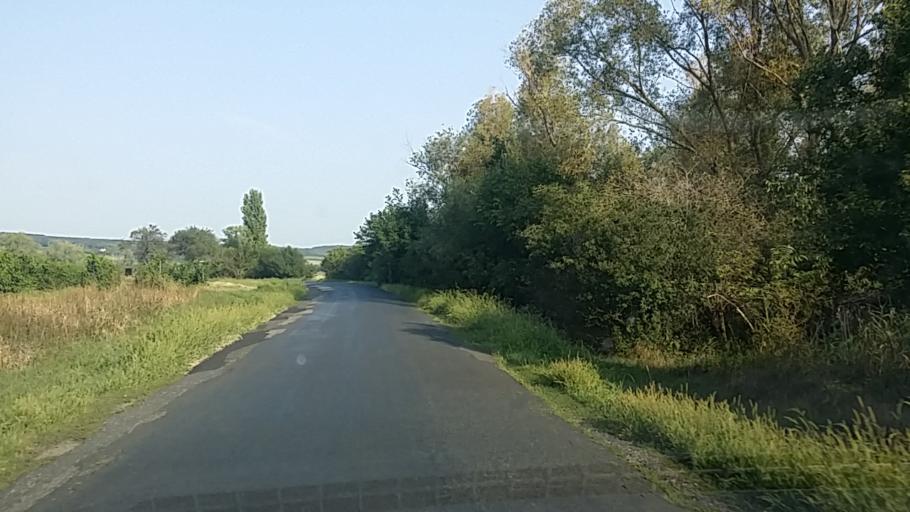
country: HU
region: Gyor-Moson-Sopron
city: Fertorakos
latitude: 47.6796
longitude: 16.6736
